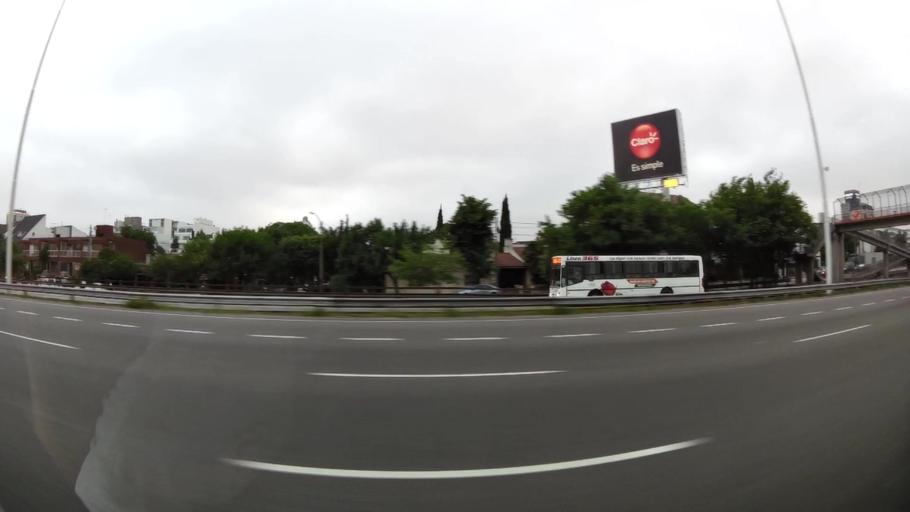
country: AR
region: Buenos Aires
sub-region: Partido de Vicente Lopez
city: Olivos
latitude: -34.5424
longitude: -58.4833
